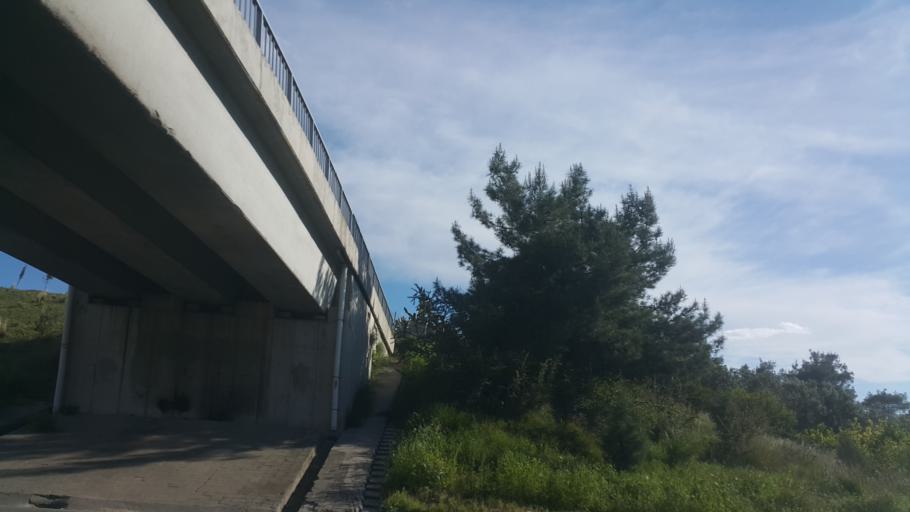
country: TR
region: Adana
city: Yakapinar
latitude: 36.9989
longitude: 35.5630
